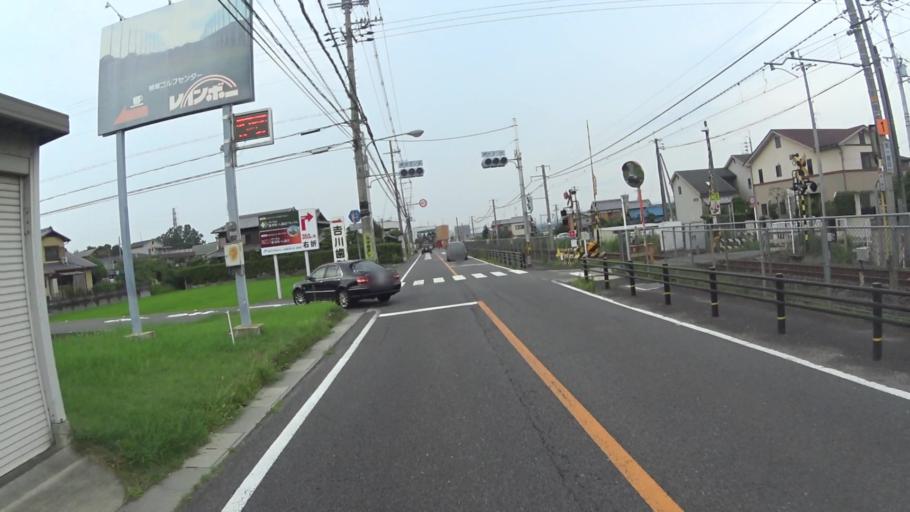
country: JP
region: Kyoto
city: Tanabe
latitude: 34.7820
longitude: 135.7882
